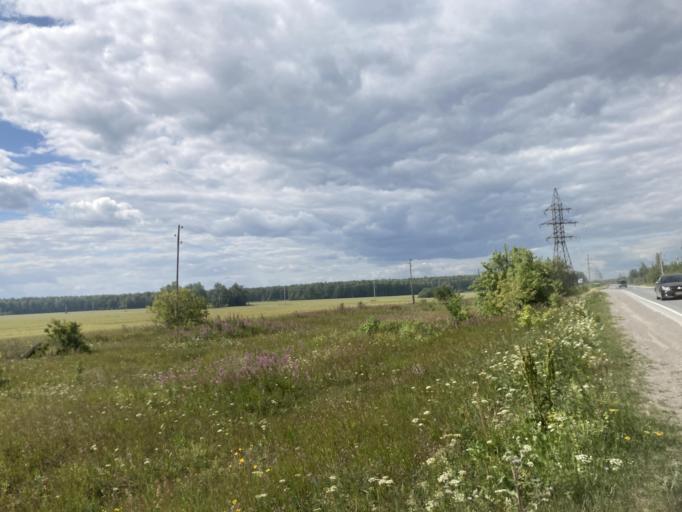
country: RU
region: Sverdlovsk
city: Bogdanovich
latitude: 56.8001
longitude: 62.0384
